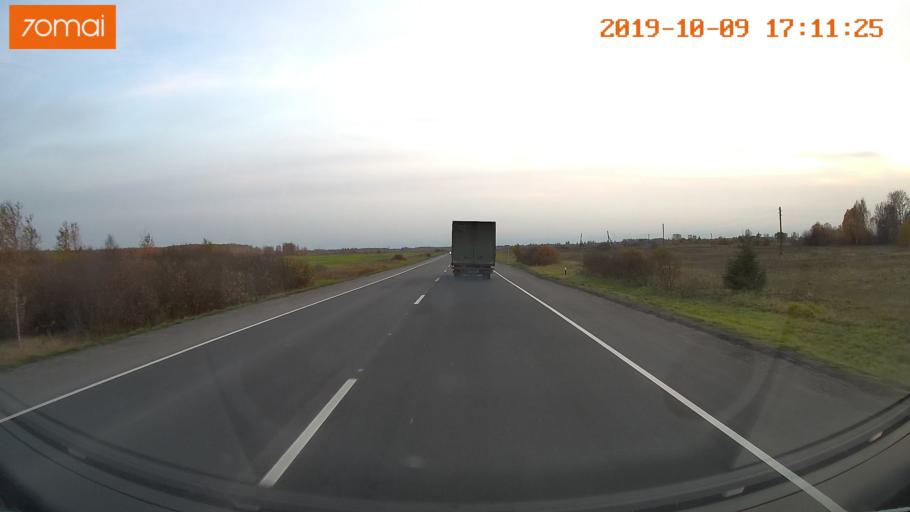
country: RU
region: Ivanovo
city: Privolzhsk
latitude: 57.3432
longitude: 41.2503
